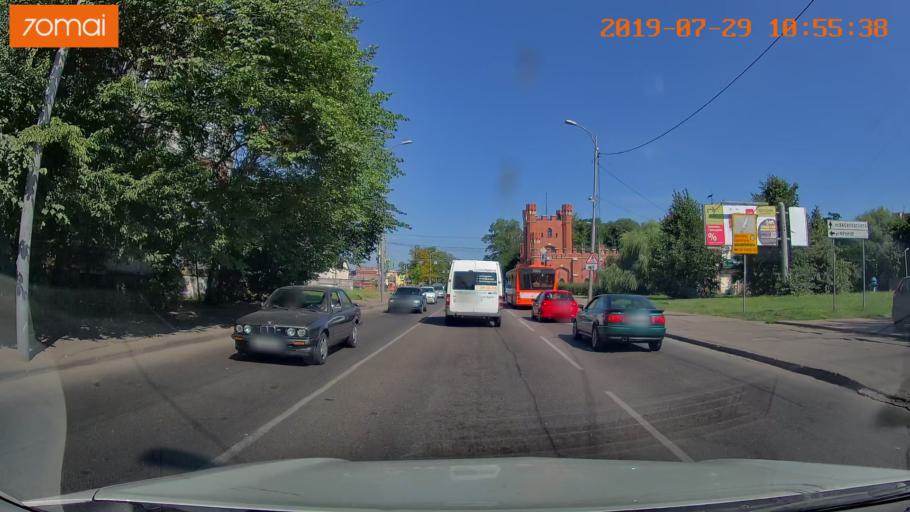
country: RU
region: Kaliningrad
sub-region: Gorod Kaliningrad
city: Kaliningrad
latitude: 54.7127
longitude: 20.5364
